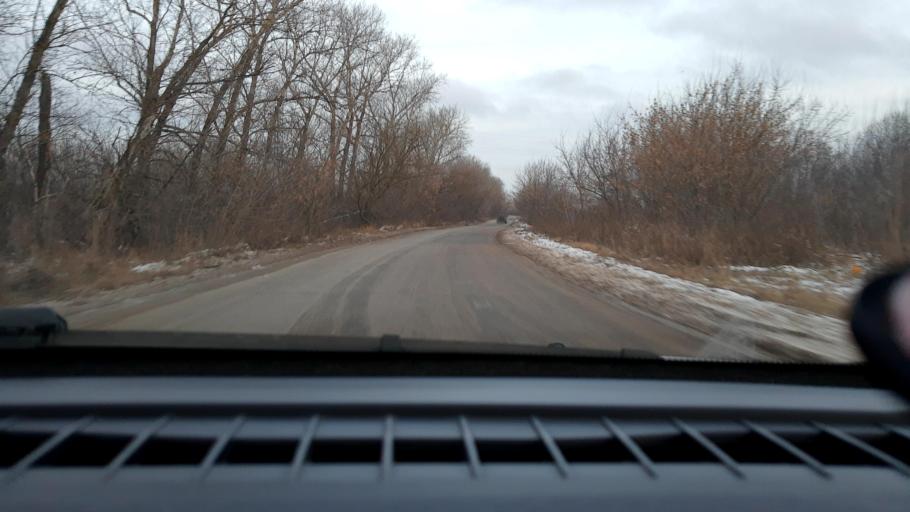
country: RU
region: Nizjnij Novgorod
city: Gorbatovka
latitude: 56.2509
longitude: 43.7557
